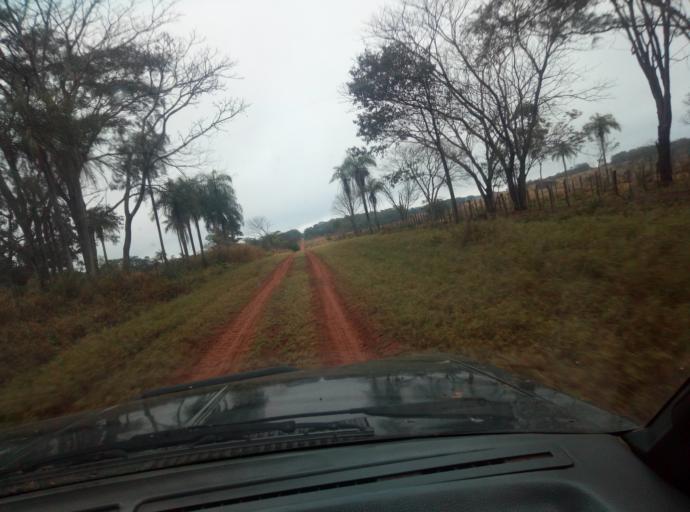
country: PY
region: Caaguazu
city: Carayao
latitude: -25.1934
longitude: -56.3305
